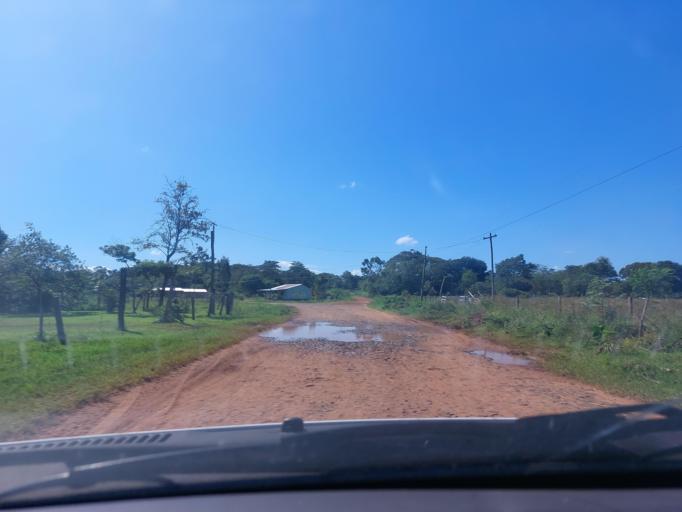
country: PY
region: San Pedro
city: Itacurubi del Rosario
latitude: -24.5841
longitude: -56.6001
